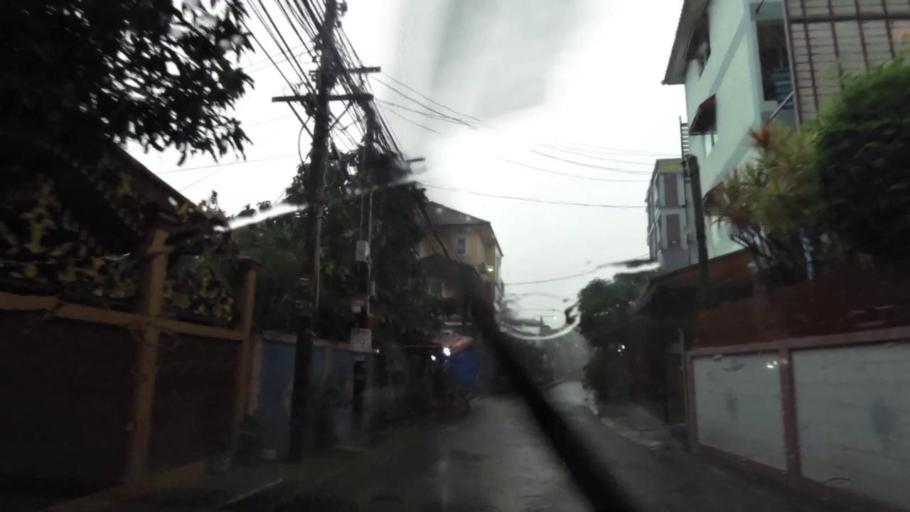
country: TH
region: Bangkok
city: Phra Khanong
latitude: 13.7152
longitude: 100.5976
